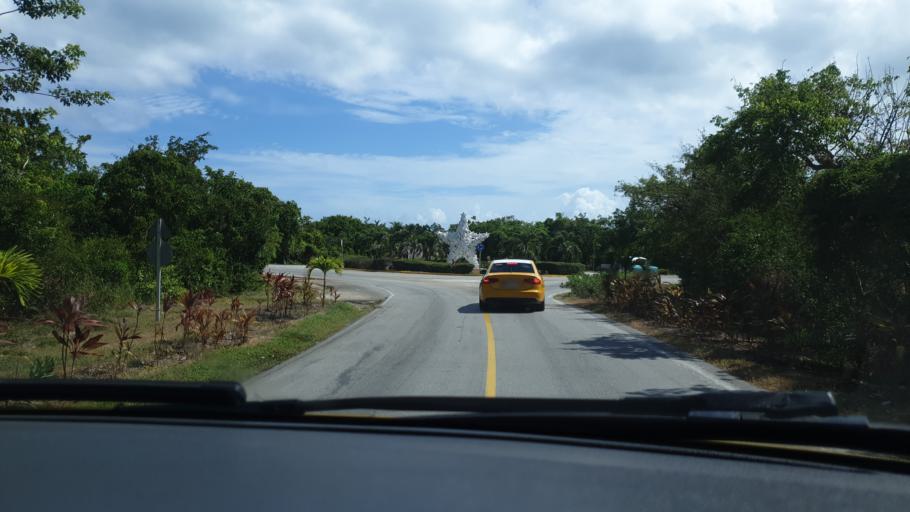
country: CU
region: Sancti Spiritus
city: Yaguajay
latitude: 22.6554
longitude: -79.0382
